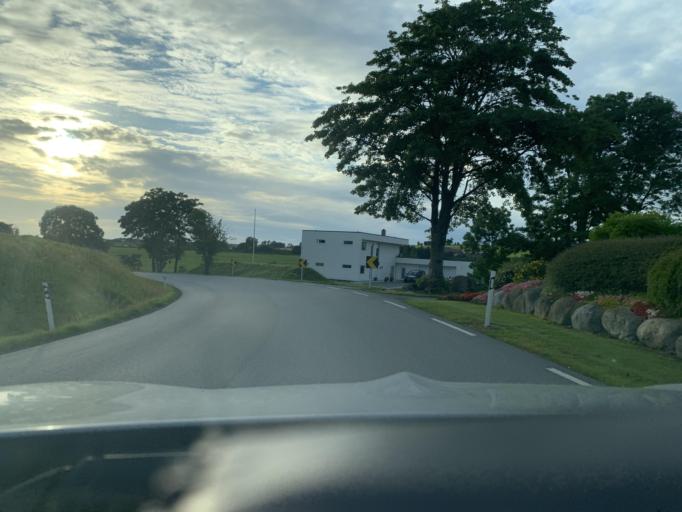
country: NO
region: Rogaland
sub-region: Time
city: Bryne
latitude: 58.7022
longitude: 5.7030
